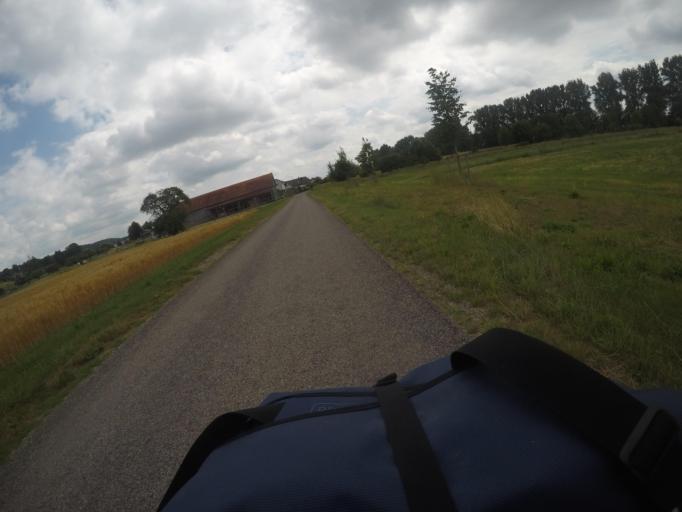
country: DE
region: Bavaria
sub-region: Swabia
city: Heimertingen
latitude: 48.0199
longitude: 10.1724
